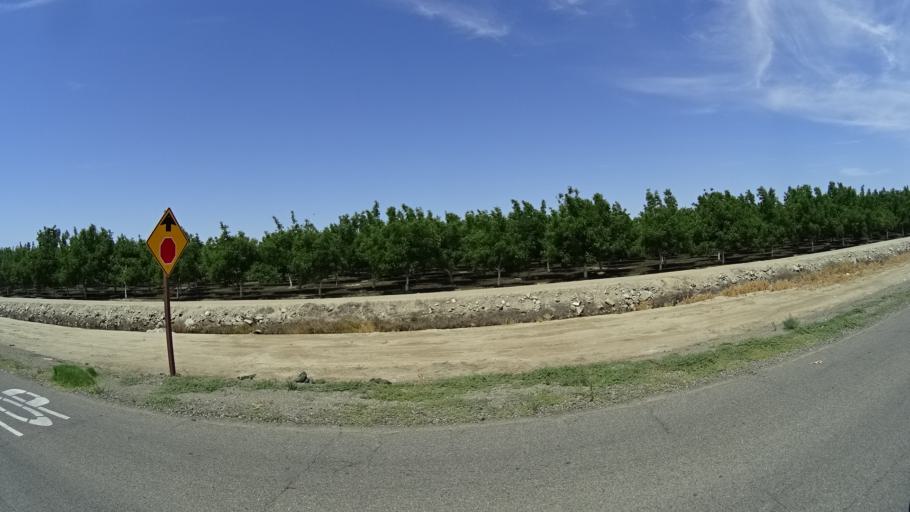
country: US
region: California
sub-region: Kings County
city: Lucerne
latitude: 36.3733
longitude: -119.6914
